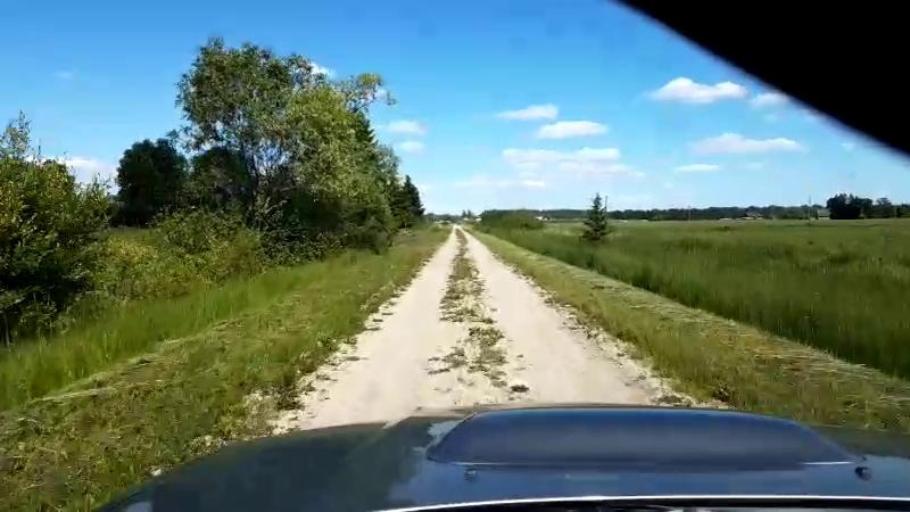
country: EE
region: Paernumaa
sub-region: Halinga vald
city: Parnu-Jaagupi
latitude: 58.5192
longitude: 24.5153
